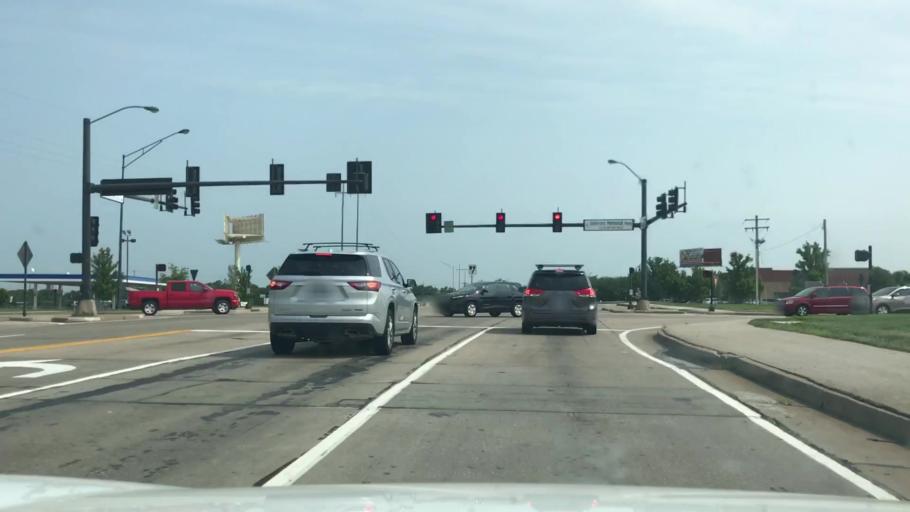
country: US
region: Missouri
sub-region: Saint Charles County
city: Dardenne Prairie
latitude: 38.7999
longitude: -90.7345
